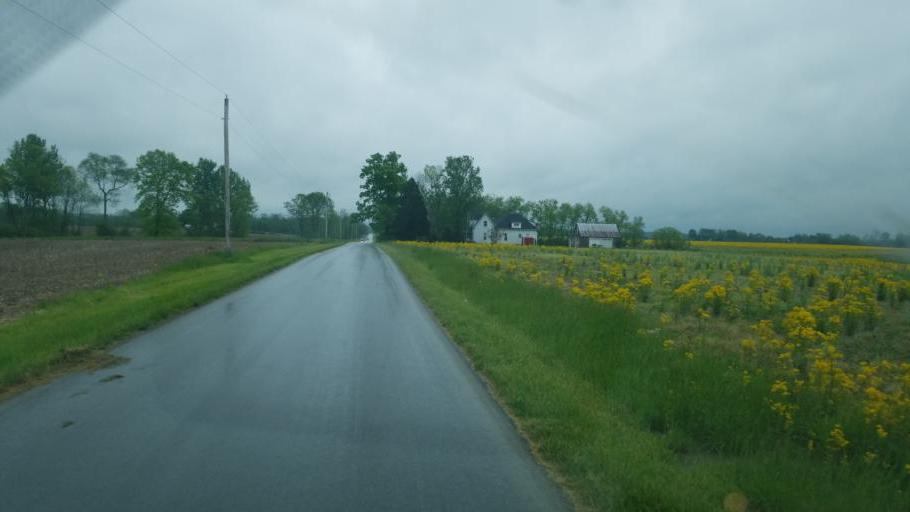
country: US
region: Ohio
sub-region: Highland County
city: Greenfield
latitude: 39.3291
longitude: -83.4303
